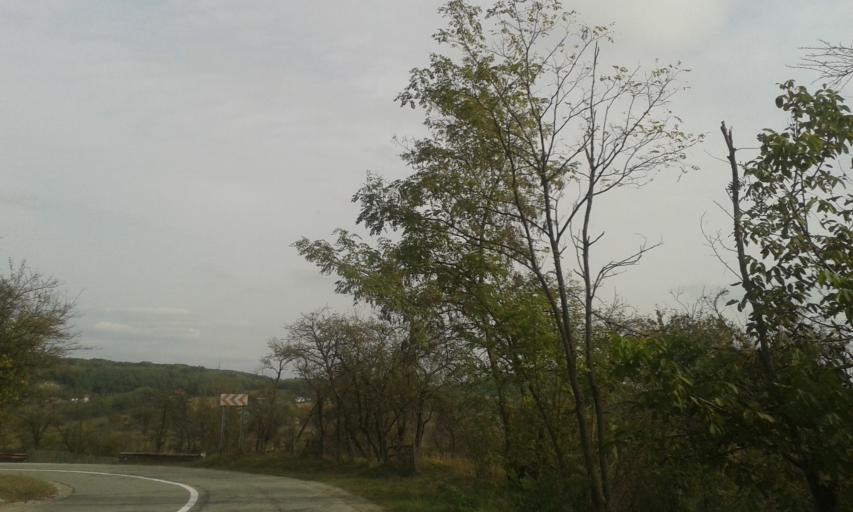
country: RO
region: Valcea
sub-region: Comuna Gradistea
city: Gradistea
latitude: 44.9150
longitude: 23.7753
